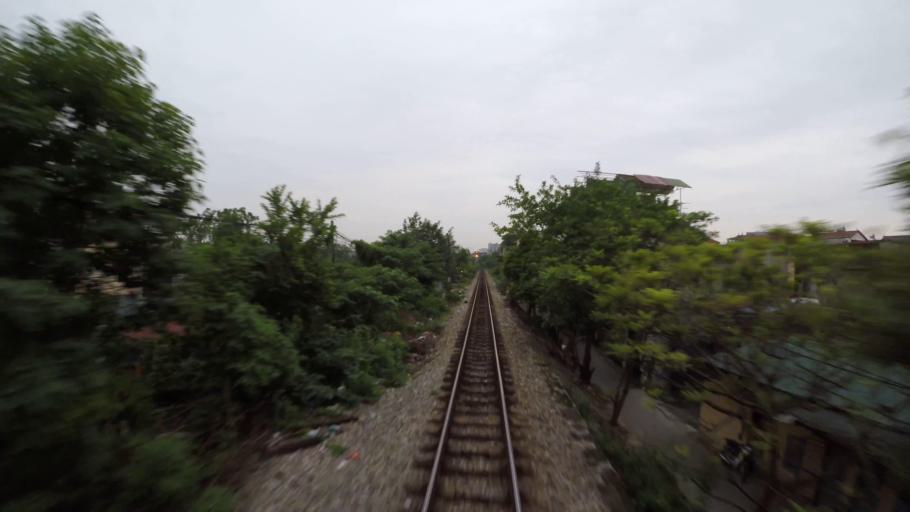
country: VN
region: Ha Noi
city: Trau Quy
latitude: 21.0413
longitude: 105.8971
